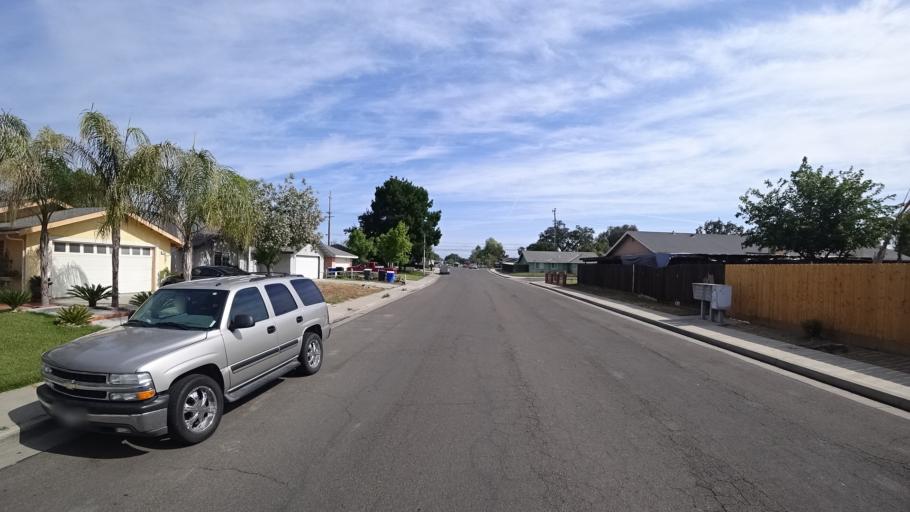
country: US
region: California
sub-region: Kings County
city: Hanford
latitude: 36.3125
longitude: -119.6650
